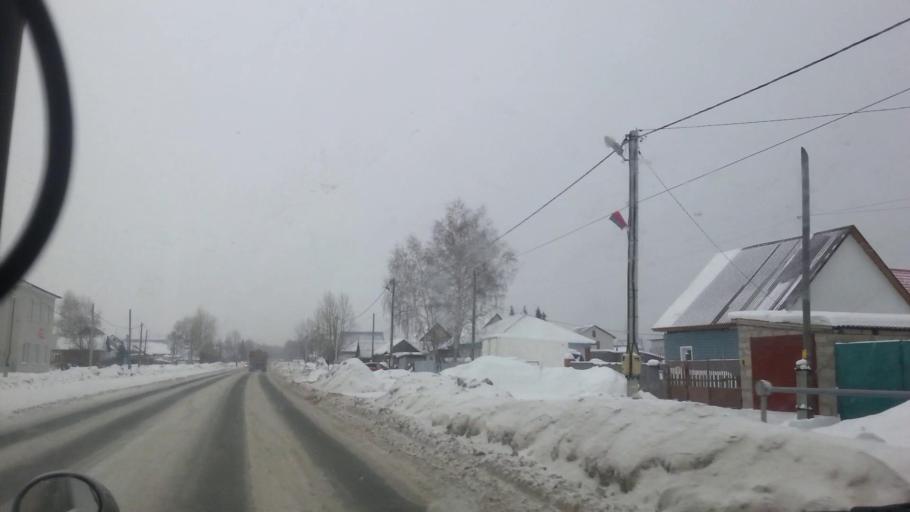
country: RU
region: Altai Krai
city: Vlasikha
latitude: 53.2971
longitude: 83.5838
